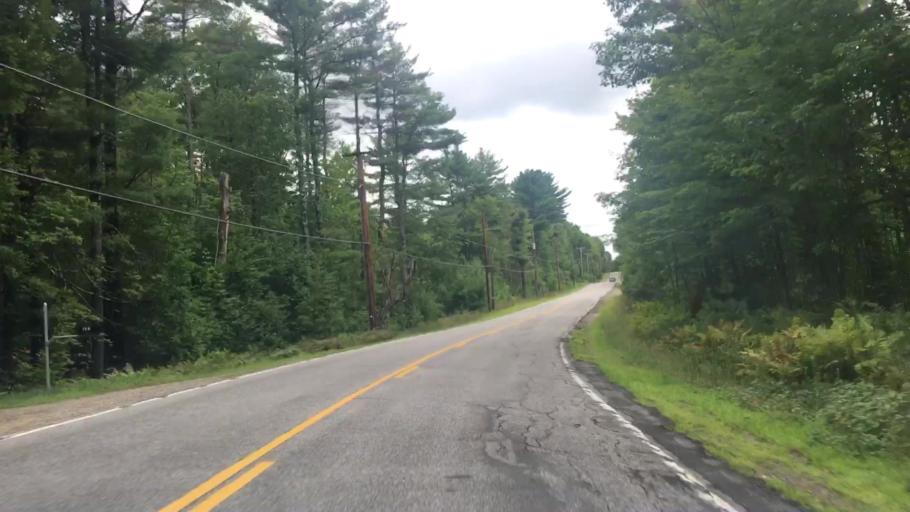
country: US
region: Maine
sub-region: York County
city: Limerick
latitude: 43.6725
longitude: -70.7777
